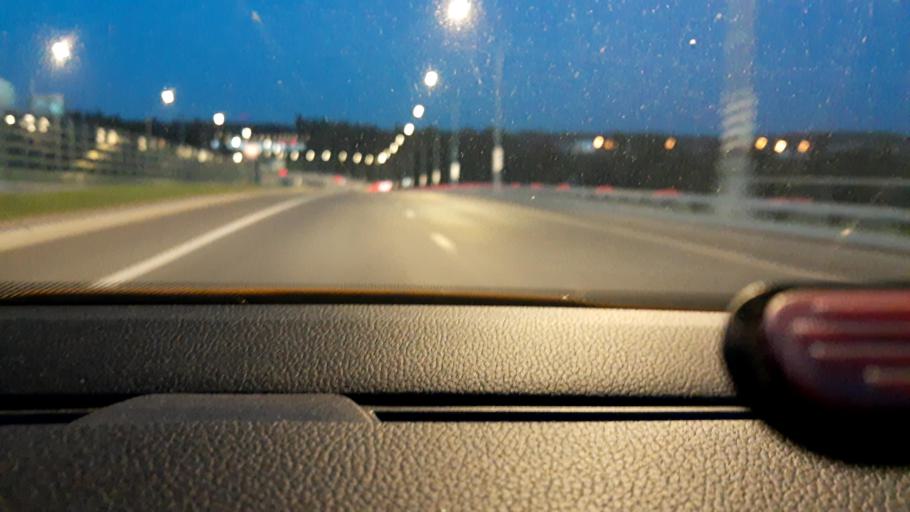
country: RU
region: Moskovskaya
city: Filimonki
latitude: 55.5640
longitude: 37.3449
